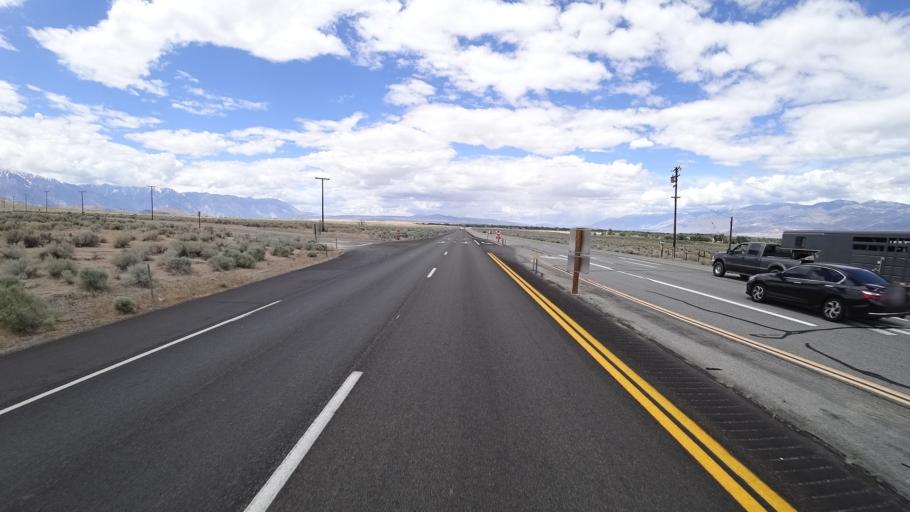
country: US
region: California
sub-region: Inyo County
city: Bishop
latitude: 37.3177
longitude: -118.3874
